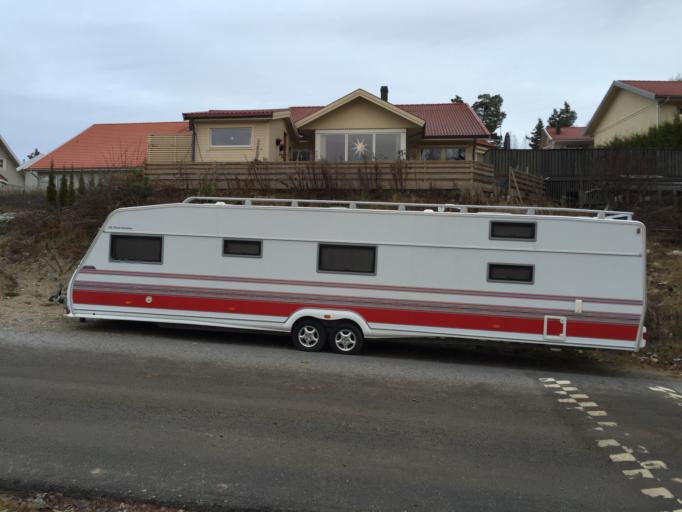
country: SE
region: Stockholm
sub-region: Botkyrka Kommun
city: Varsta
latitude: 59.2046
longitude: 17.7872
